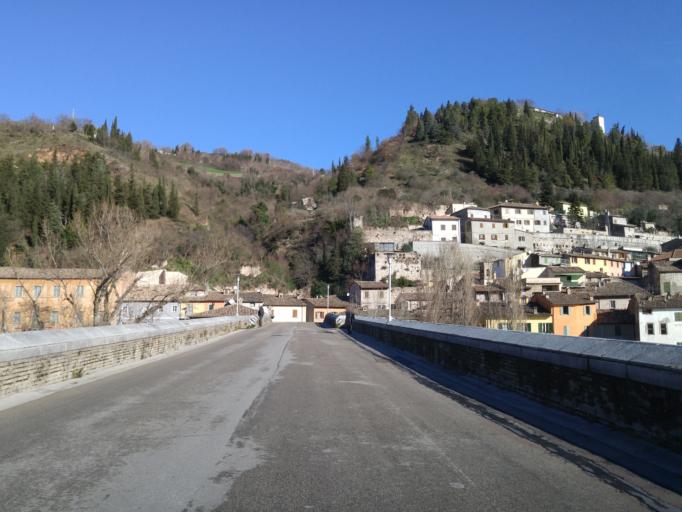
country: IT
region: The Marches
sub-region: Provincia di Pesaro e Urbino
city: Fossombrone
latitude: 43.6877
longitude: 12.8032
